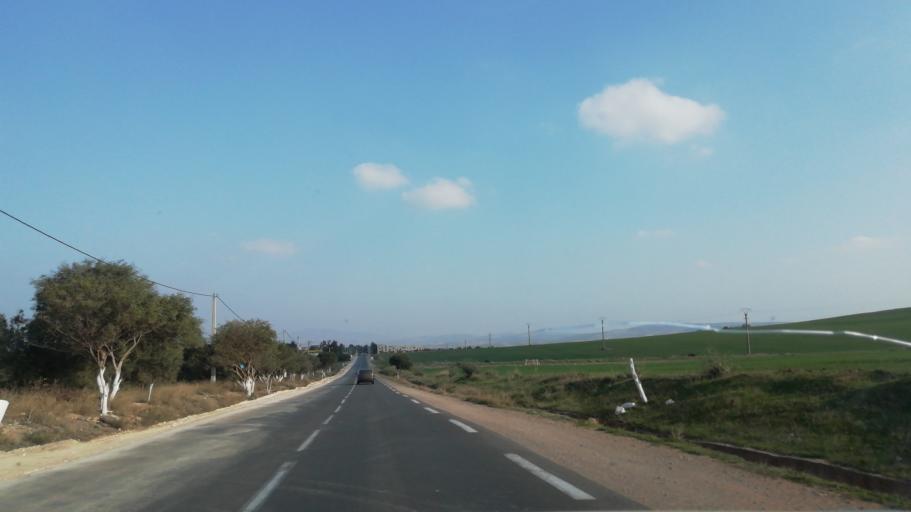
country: DZ
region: Ain Temouchent
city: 'Ain Temouchent
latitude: 35.3039
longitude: -1.0391
